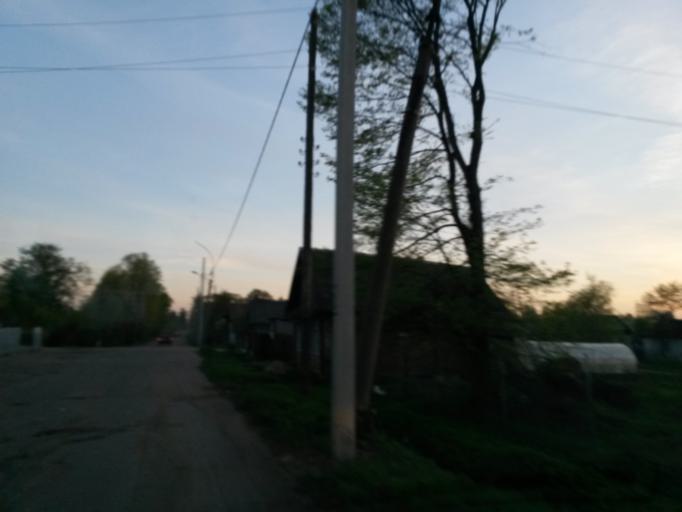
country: RU
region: Jaroslavl
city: Tutayev
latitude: 57.8860
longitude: 39.5499
